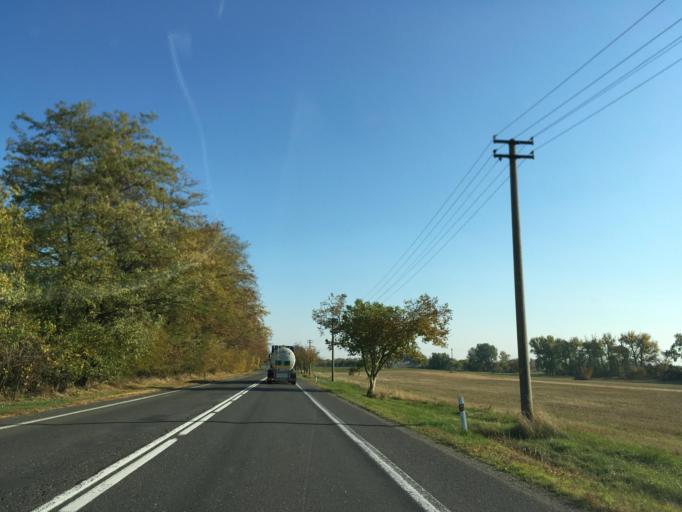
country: HU
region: Komarom-Esztergom
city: Acs
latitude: 47.7860
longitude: 17.9176
